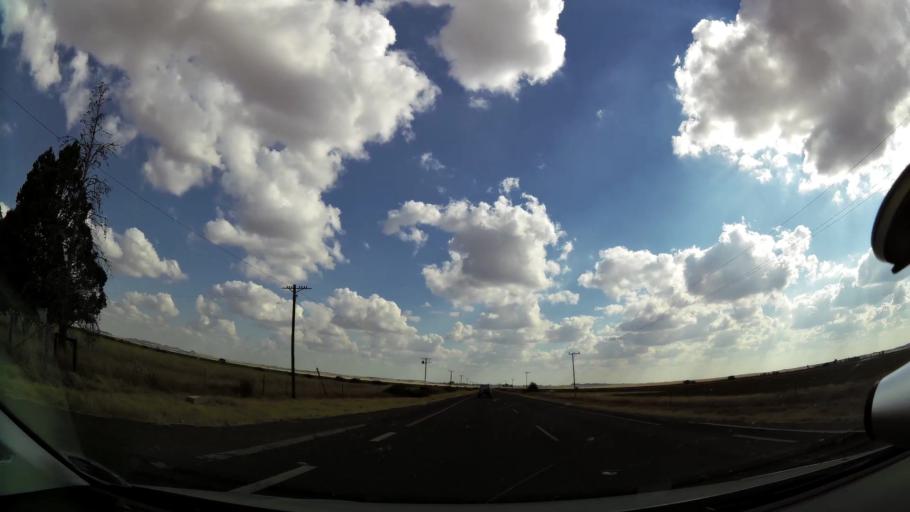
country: ZA
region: Orange Free State
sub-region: Xhariep District Municipality
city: Koffiefontein
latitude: -29.1311
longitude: 25.5258
